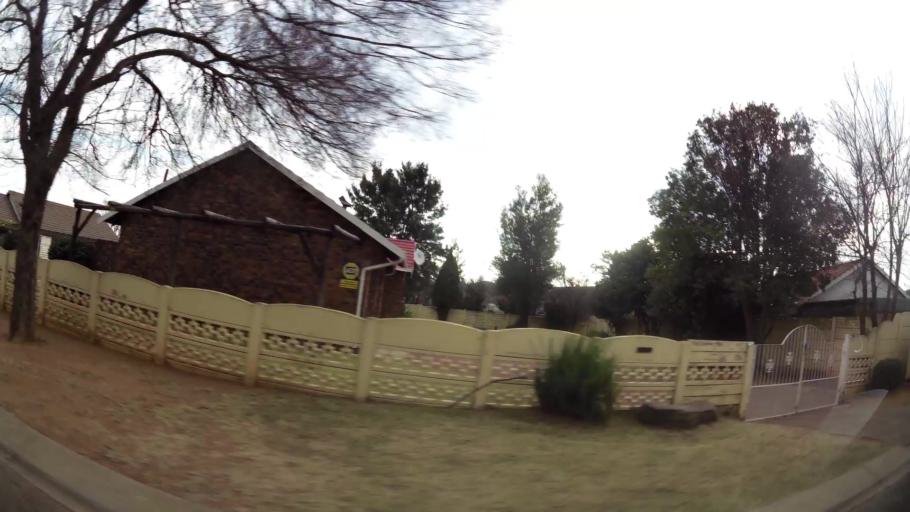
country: ZA
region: Gauteng
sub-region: Ekurhuleni Metropolitan Municipality
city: Benoni
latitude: -26.1267
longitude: 28.3616
